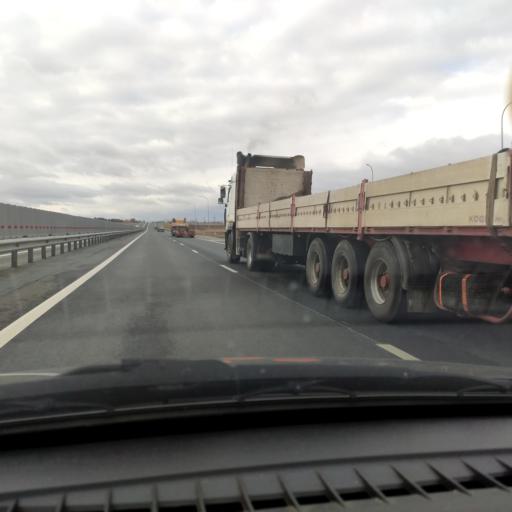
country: RU
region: Samara
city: Mirnyy
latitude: 53.4582
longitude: 50.2188
